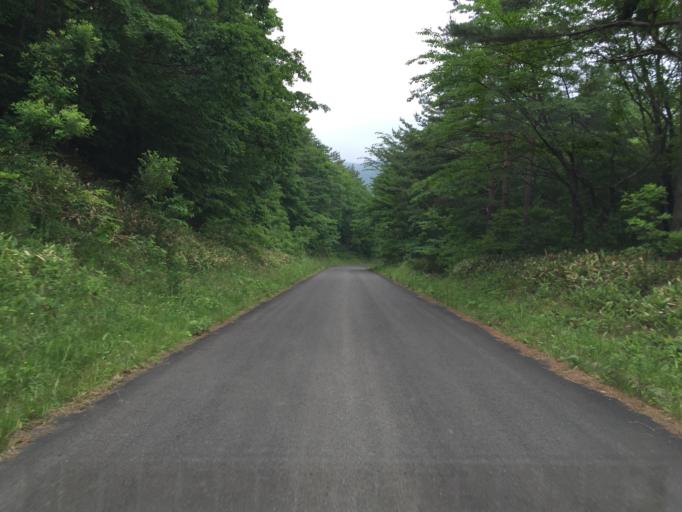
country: JP
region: Fukushima
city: Yanagawamachi-saiwaicho
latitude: 37.7912
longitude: 140.6879
